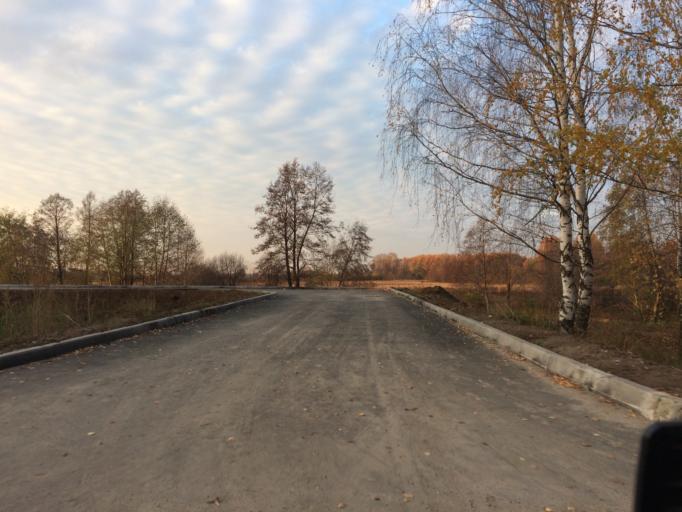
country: RU
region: Mariy-El
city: Yoshkar-Ola
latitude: 56.6443
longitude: 47.9288
